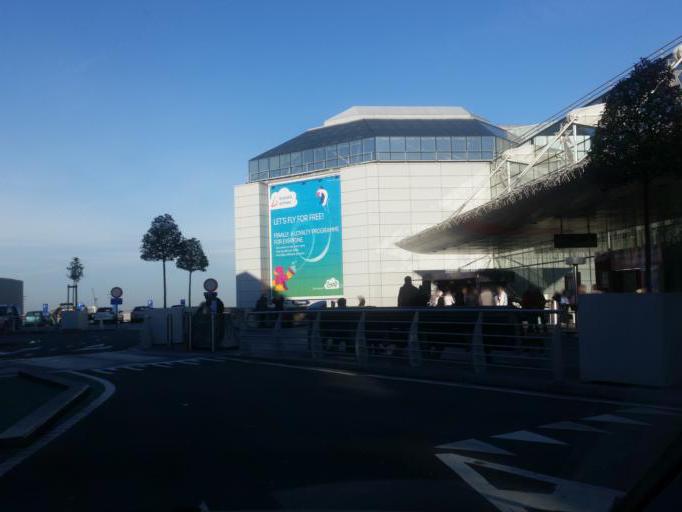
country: BE
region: Flanders
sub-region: Provincie Vlaams-Brabant
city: Zaventem
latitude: 50.8978
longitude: 4.4829
